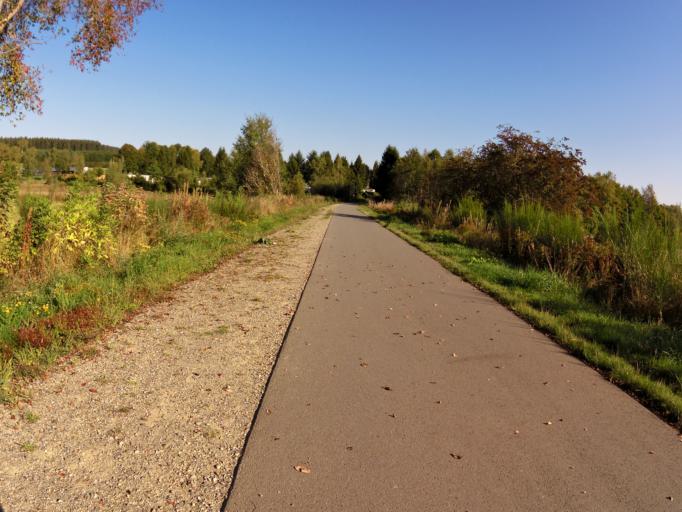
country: BE
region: Wallonia
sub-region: Province de Liege
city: Ambleve
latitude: 50.3453
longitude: 6.1204
